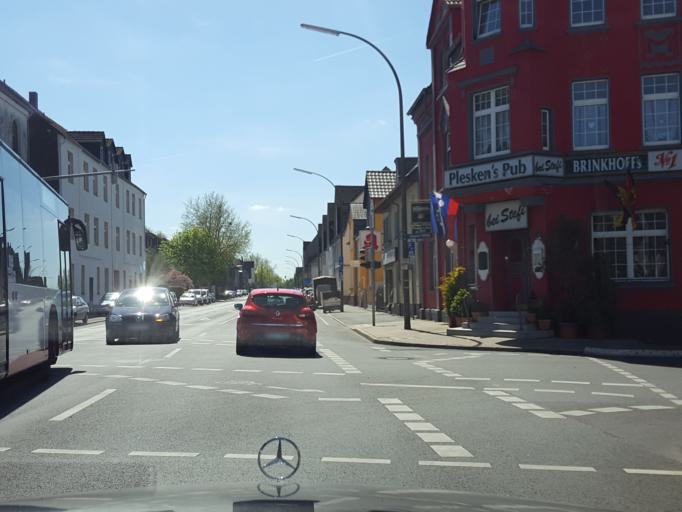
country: DE
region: North Rhine-Westphalia
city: Castrop-Rauxel
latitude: 51.5025
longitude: 7.3251
